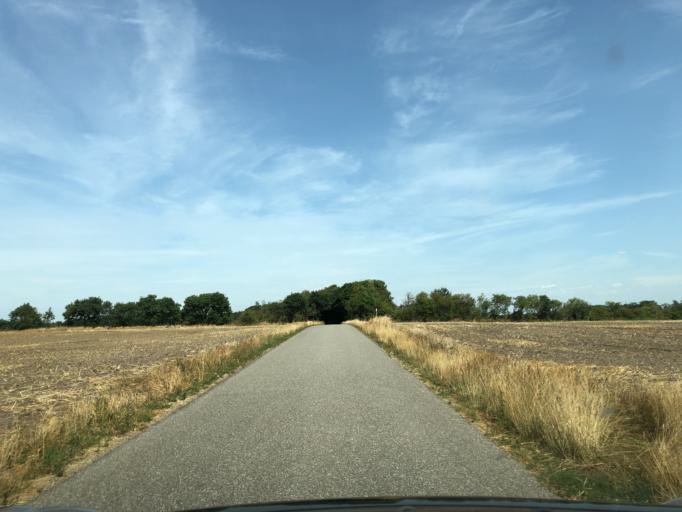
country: DK
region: Central Jutland
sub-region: Ringkobing-Skjern Kommune
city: Skjern
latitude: 55.9746
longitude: 8.4891
